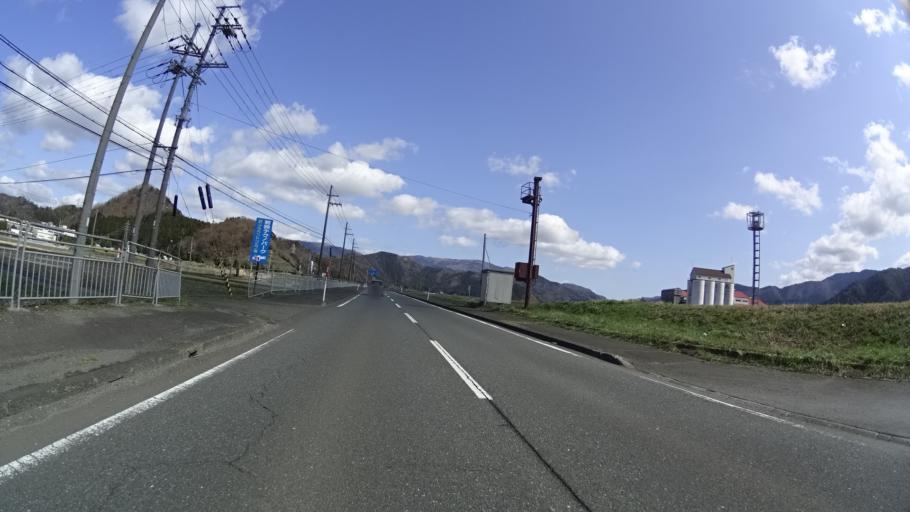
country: JP
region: Fukui
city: Obama
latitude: 35.4692
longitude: 135.8527
